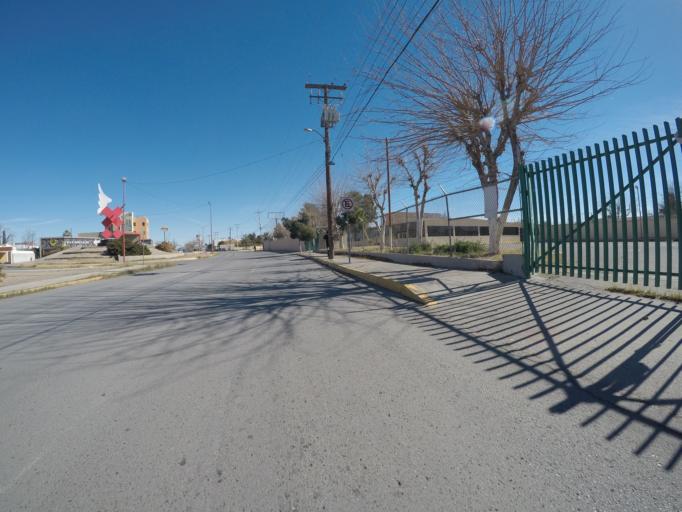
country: MX
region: Chihuahua
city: Ciudad Juarez
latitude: 31.7410
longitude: -106.4442
